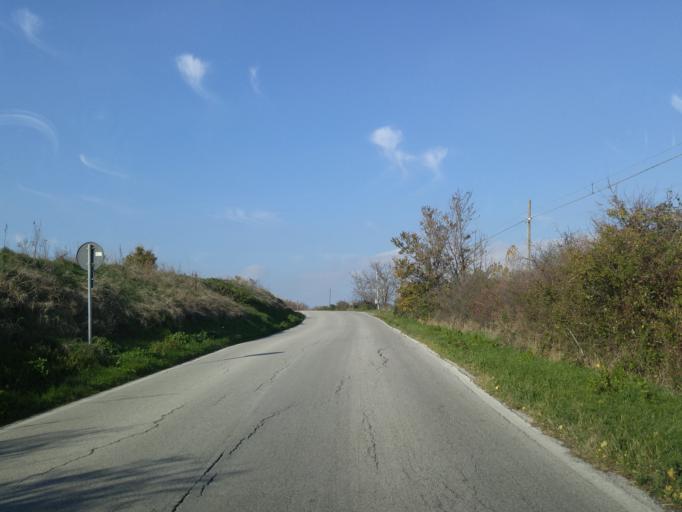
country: IT
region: The Marches
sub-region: Provincia di Pesaro e Urbino
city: Lucrezia
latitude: 43.7970
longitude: 12.9173
